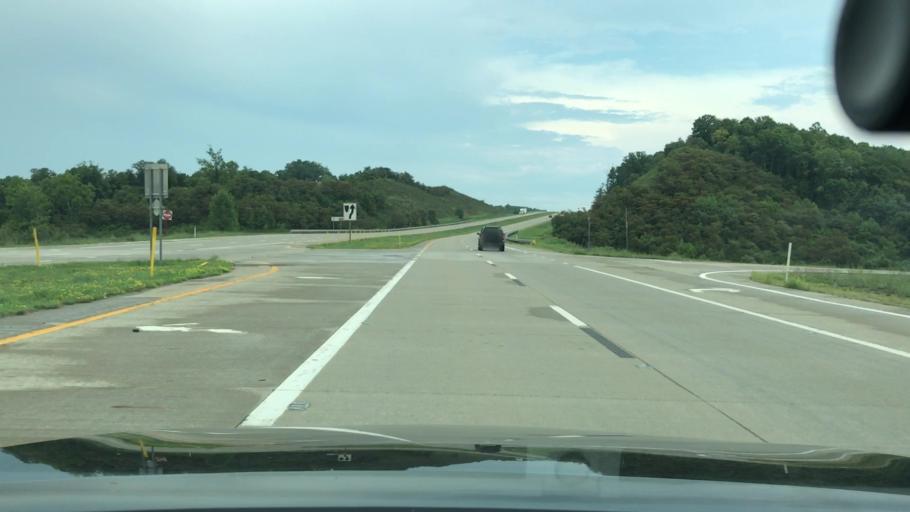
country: US
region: West Virginia
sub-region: Mason County
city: Point Pleasant
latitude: 38.7705
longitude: -82.0370
